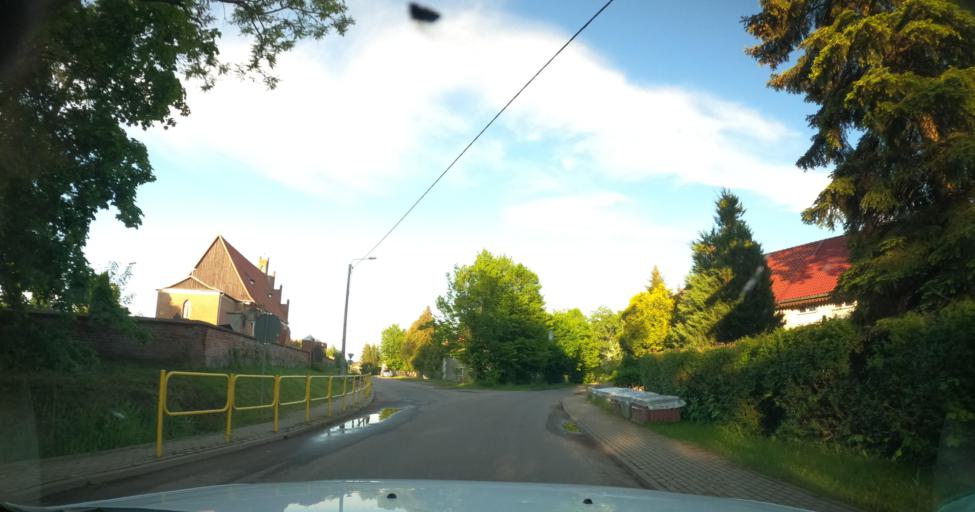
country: PL
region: Warmian-Masurian Voivodeship
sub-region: Powiat lidzbarski
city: Orneta
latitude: 54.1760
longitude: 20.1549
